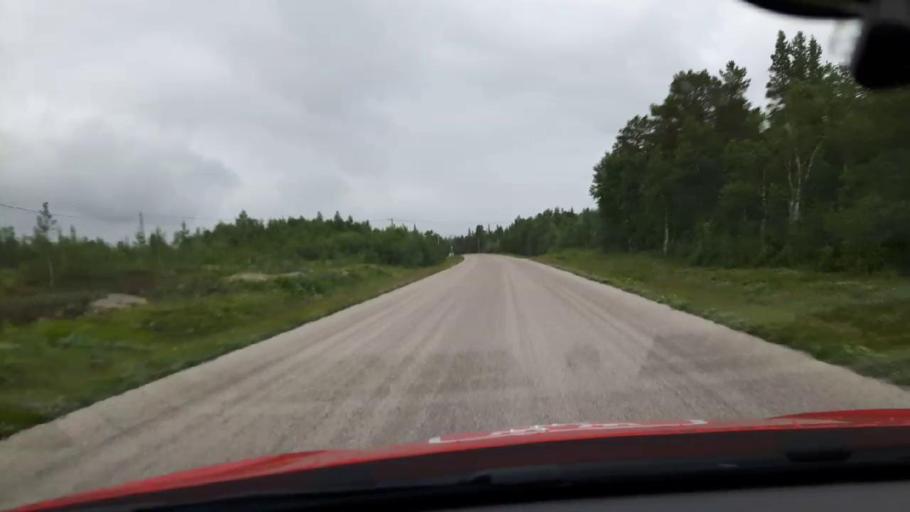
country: NO
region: Nord-Trondelag
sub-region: Meraker
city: Meraker
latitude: 63.2672
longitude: 12.3882
